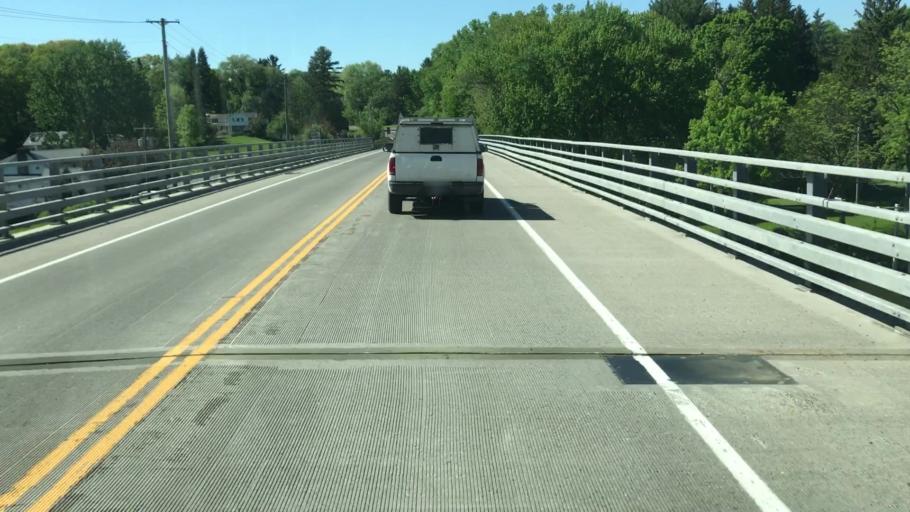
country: US
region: New York
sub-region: Onondaga County
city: Seneca Knolls
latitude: 43.1300
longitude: -76.2532
